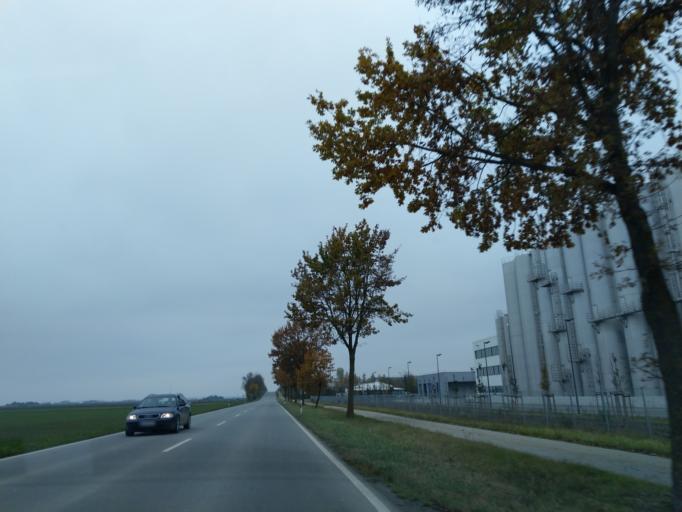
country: DE
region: Bavaria
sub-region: Lower Bavaria
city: Plattling
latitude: 48.7950
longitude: 12.8544
